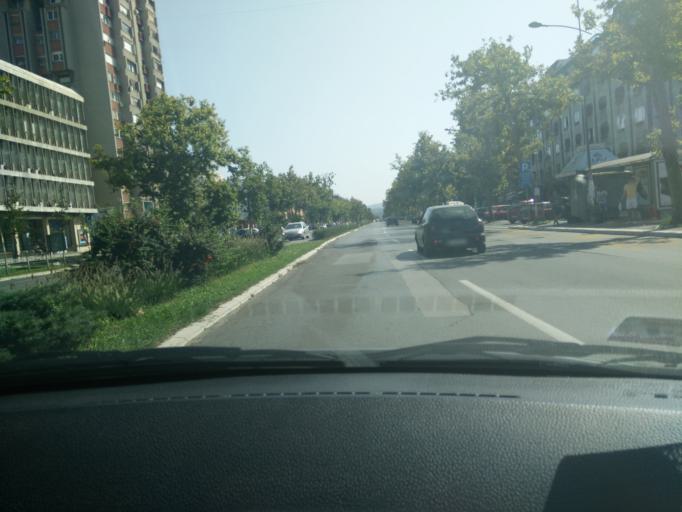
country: RS
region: Autonomna Pokrajina Vojvodina
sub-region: Juznobacki Okrug
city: Novi Sad
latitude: 45.2637
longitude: 19.8303
